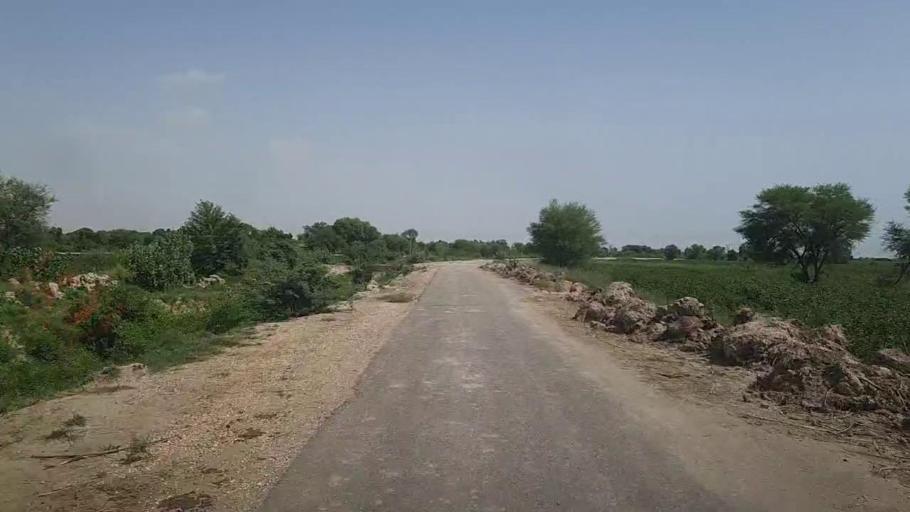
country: PK
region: Sindh
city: Pad Idan
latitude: 26.8088
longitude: 68.3310
